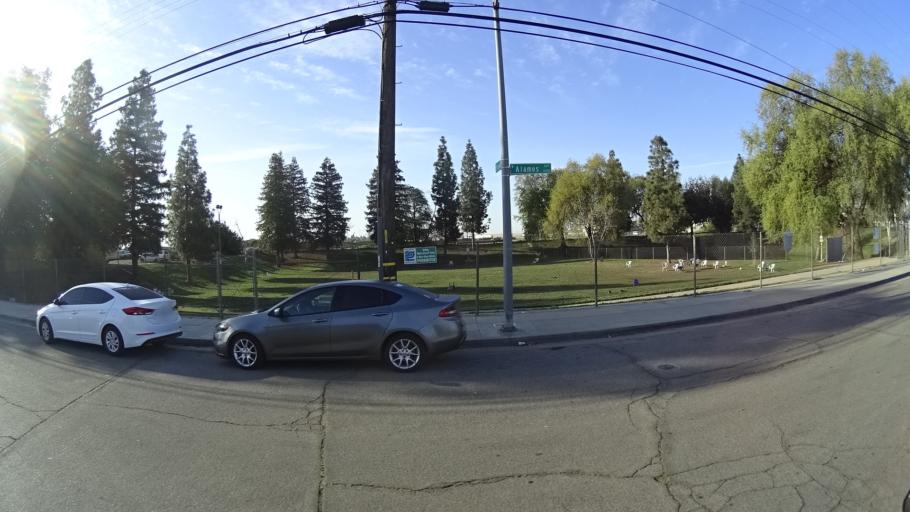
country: US
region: California
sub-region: Fresno County
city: West Park
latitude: 36.8055
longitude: -119.8685
